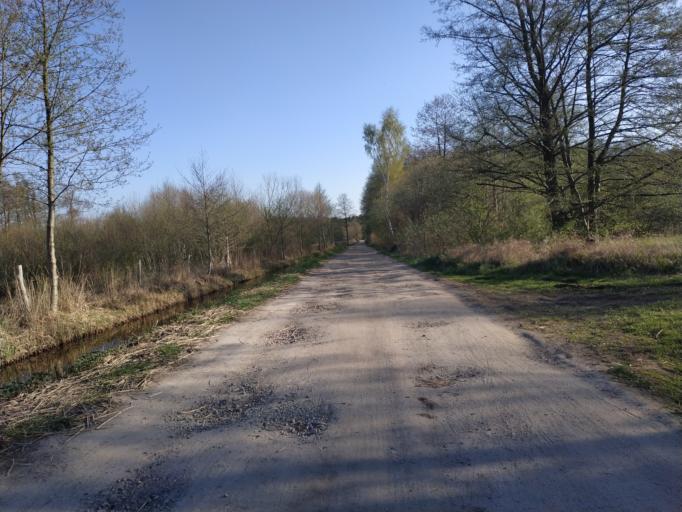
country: DE
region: Brandenburg
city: Strausberg
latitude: 52.5565
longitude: 13.8447
